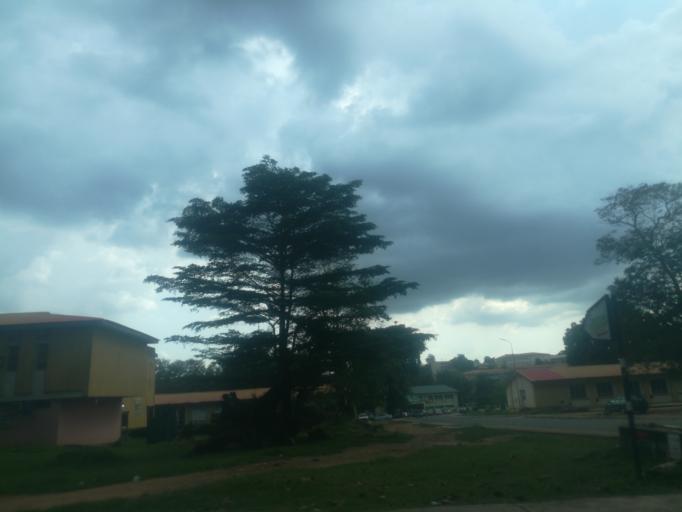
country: NG
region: Oyo
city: Ibadan
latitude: 7.4449
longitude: 3.8957
